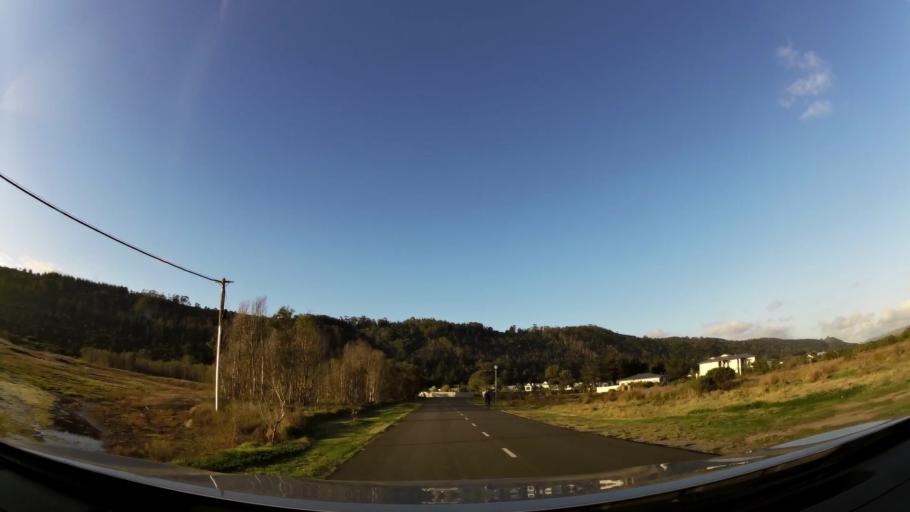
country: ZA
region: Western Cape
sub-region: Eden District Municipality
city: Knysna
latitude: -34.0133
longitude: 22.7894
